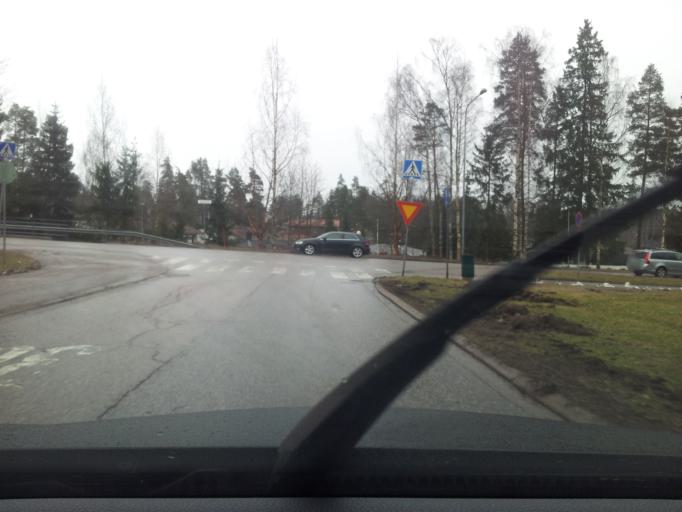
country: FI
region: Uusimaa
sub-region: Helsinki
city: Espoo
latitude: 60.1650
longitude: 24.6816
